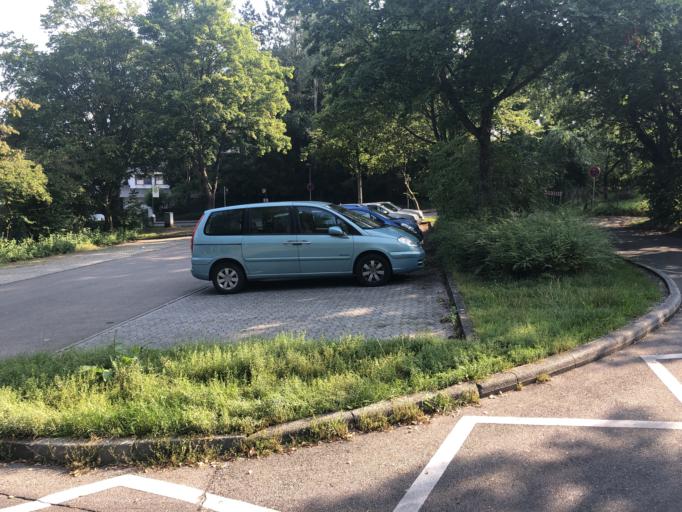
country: DE
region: Baden-Wuerttemberg
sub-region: Tuebingen Region
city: Tuebingen
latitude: 48.5127
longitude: 9.0329
